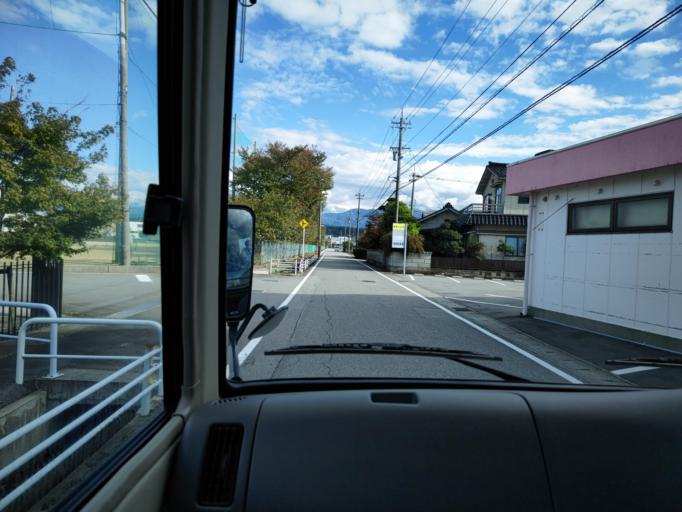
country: JP
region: Toyama
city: Uozu
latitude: 36.8703
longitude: 137.4475
